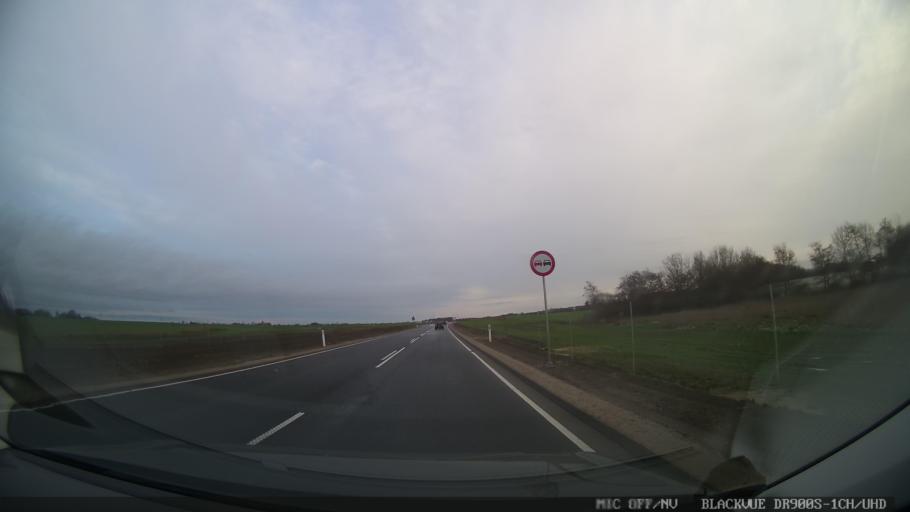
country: DK
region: Central Jutland
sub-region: Arhus Kommune
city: Tranbjerg
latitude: 56.0754
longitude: 10.1304
